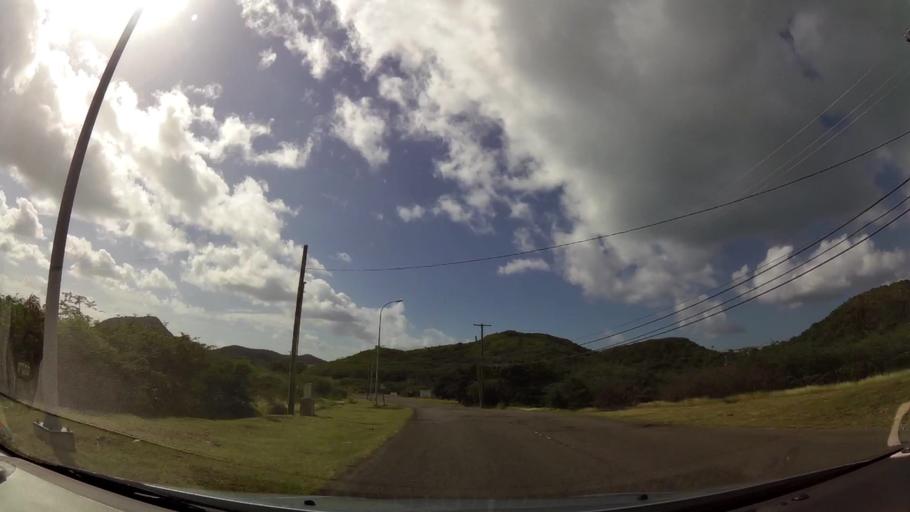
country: AG
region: Saint John
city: Saint John's
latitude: 17.1182
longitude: -61.8678
